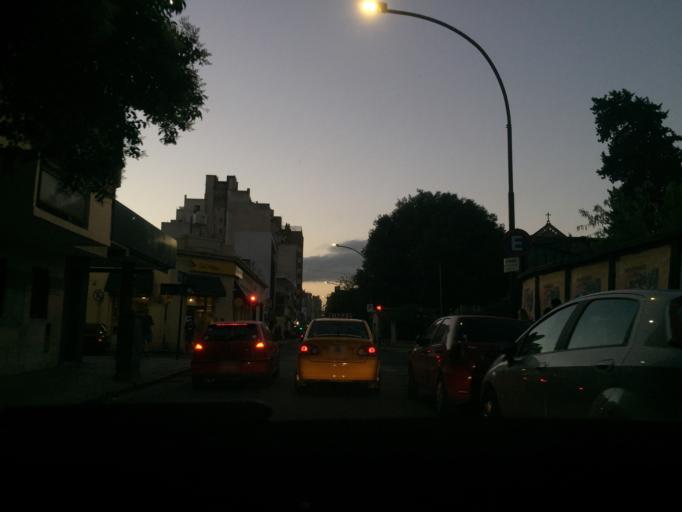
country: AR
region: Cordoba
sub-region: Departamento de Capital
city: Cordoba
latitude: -31.4114
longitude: -64.1953
